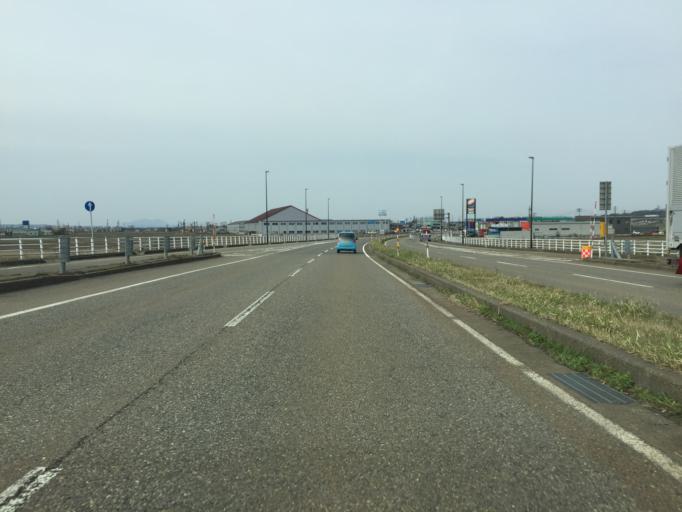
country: JP
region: Niigata
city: Nagaoka
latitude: 37.3934
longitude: 138.8370
